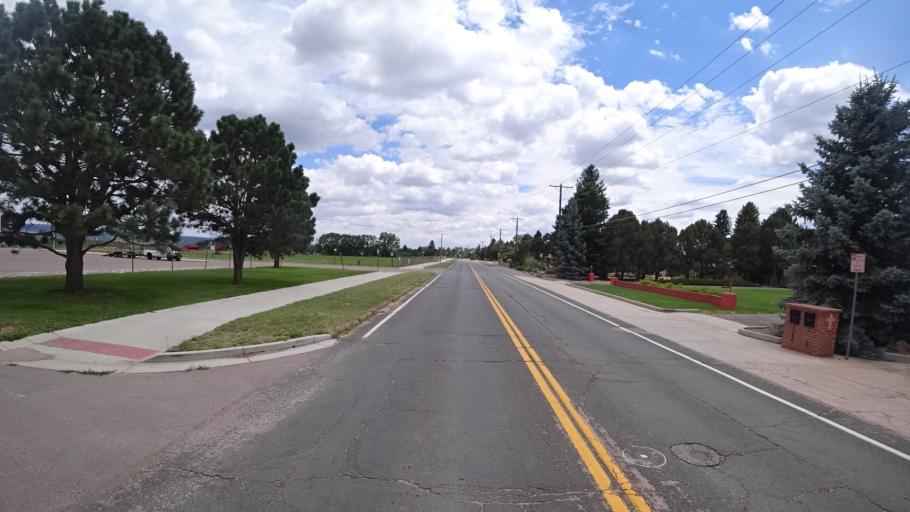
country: US
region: Colorado
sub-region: El Paso County
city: Colorado Springs
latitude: 38.8665
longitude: -104.8565
